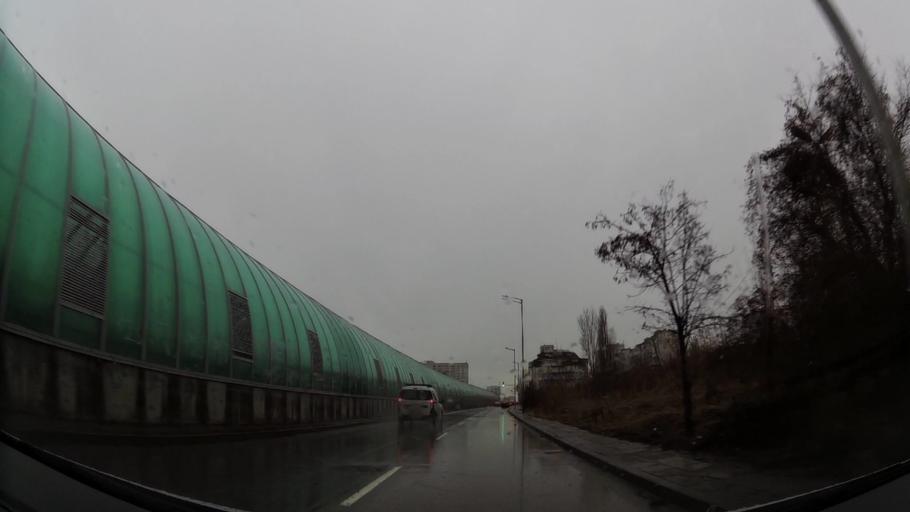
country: BG
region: Sofia-Capital
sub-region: Stolichna Obshtina
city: Sofia
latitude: 42.6559
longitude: 23.3690
